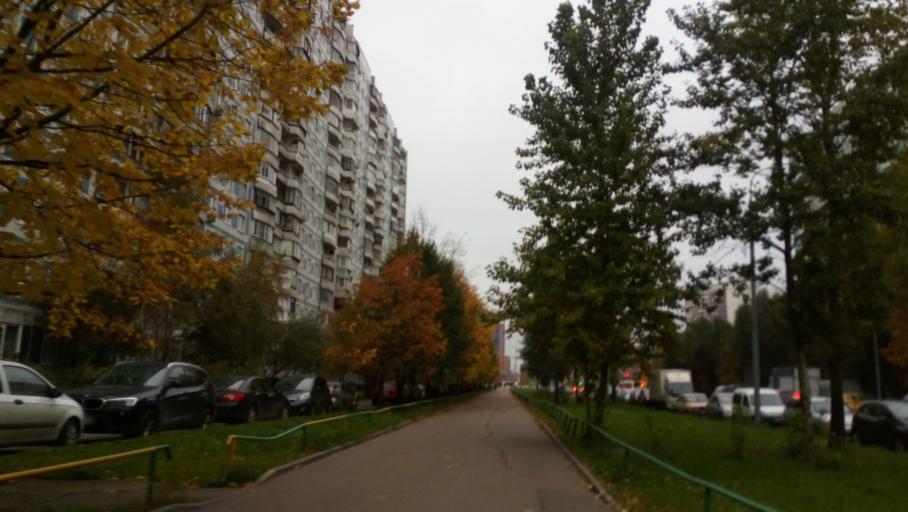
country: RU
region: Moskovskaya
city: Reutov
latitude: 55.7397
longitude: 37.8673
